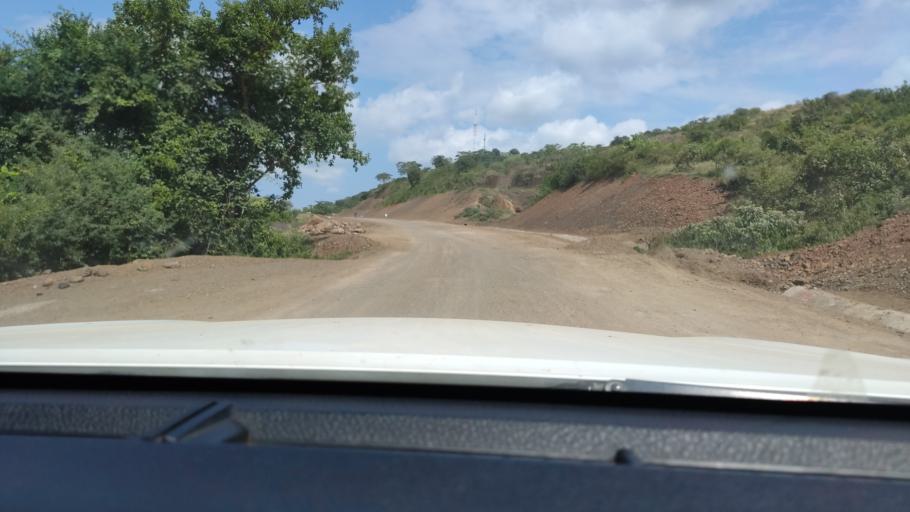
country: ET
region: Southern Nations, Nationalities, and People's Region
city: Felege Neway
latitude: 6.3909
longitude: 37.0671
